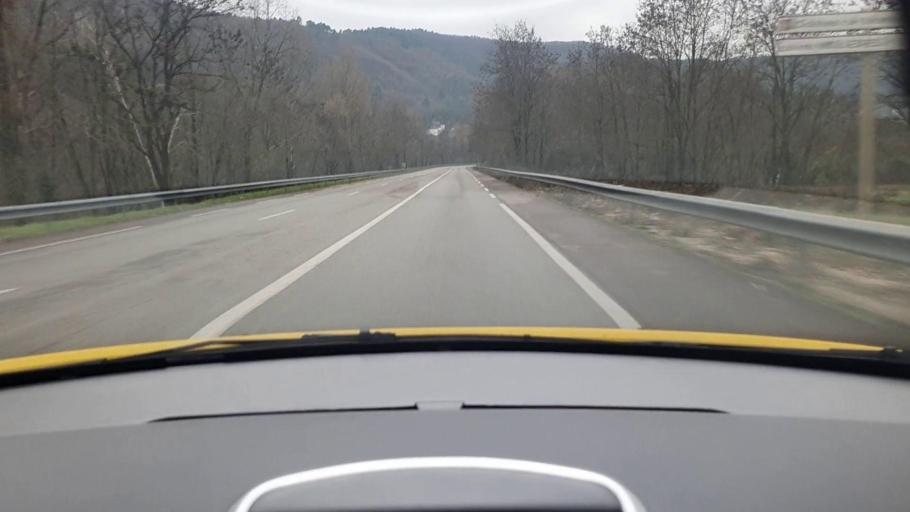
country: FR
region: Languedoc-Roussillon
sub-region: Departement du Gard
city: Molieres-sur-Ceze
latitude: 44.2667
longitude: 4.1648
